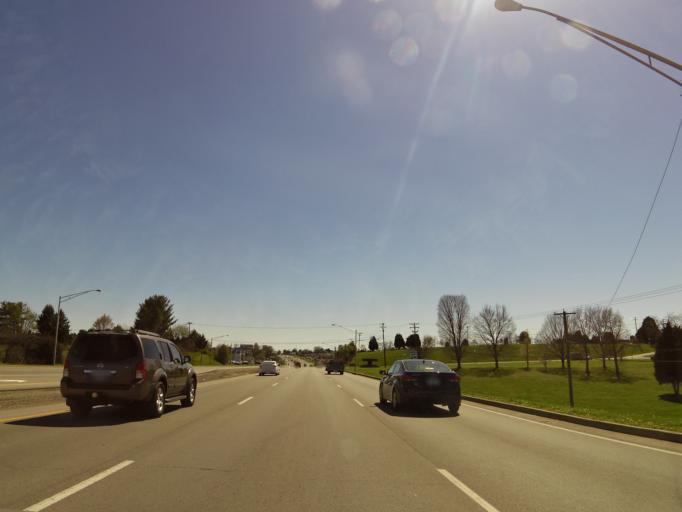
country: US
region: Kentucky
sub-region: Pulaski County
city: Somerset
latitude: 37.0616
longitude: -84.6223
